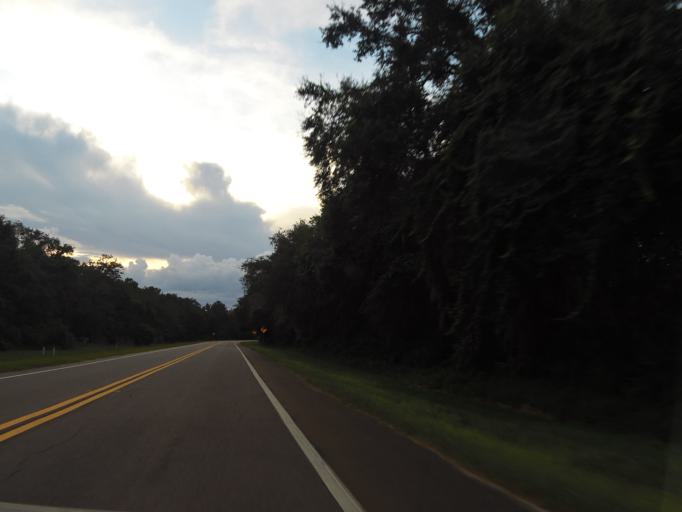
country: US
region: Florida
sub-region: Nassau County
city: Fernandina Beach
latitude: 30.6052
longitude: -81.4498
